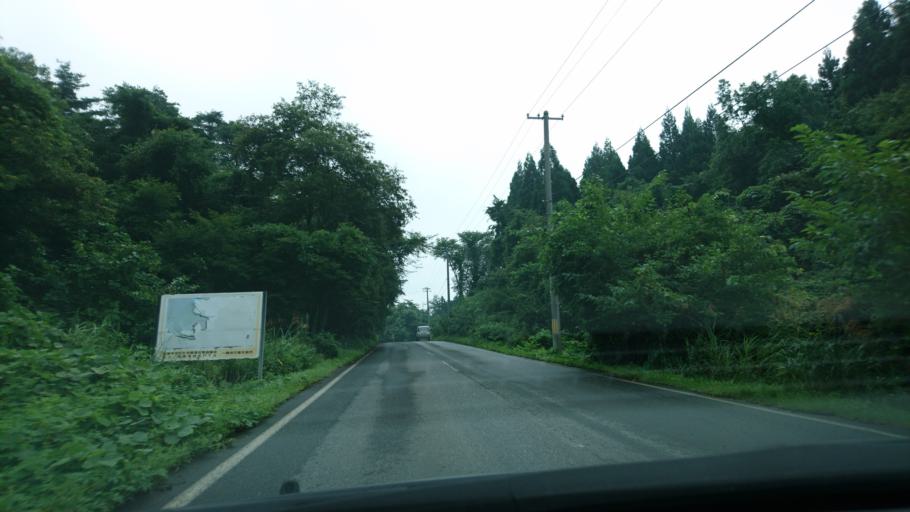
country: JP
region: Iwate
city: Ichinoseki
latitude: 38.9357
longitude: 141.1885
